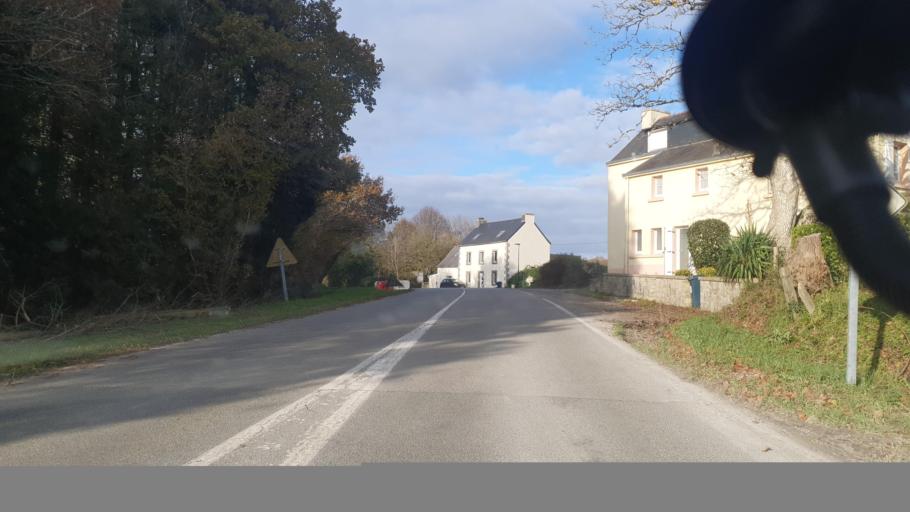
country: FR
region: Brittany
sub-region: Departement du Finistere
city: Edern
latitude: 48.1019
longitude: -3.9861
